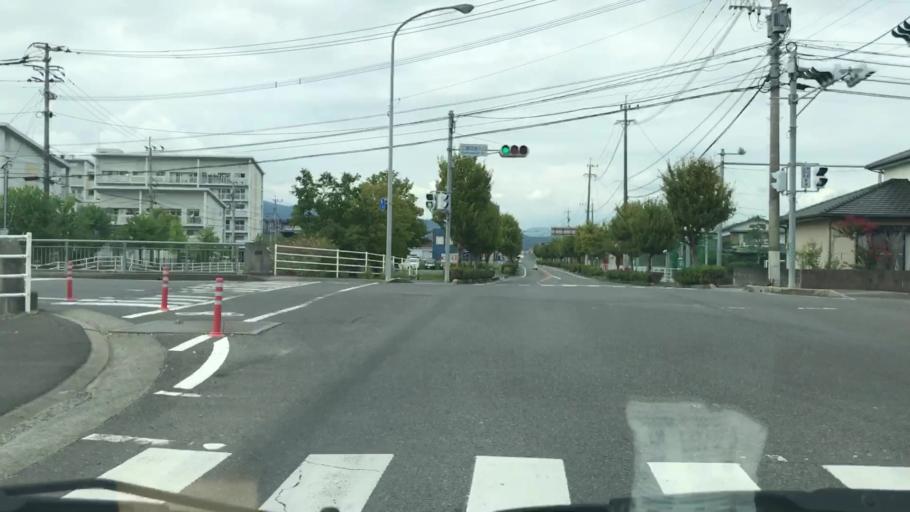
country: JP
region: Saga Prefecture
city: Saga-shi
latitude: 33.2649
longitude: 130.2625
